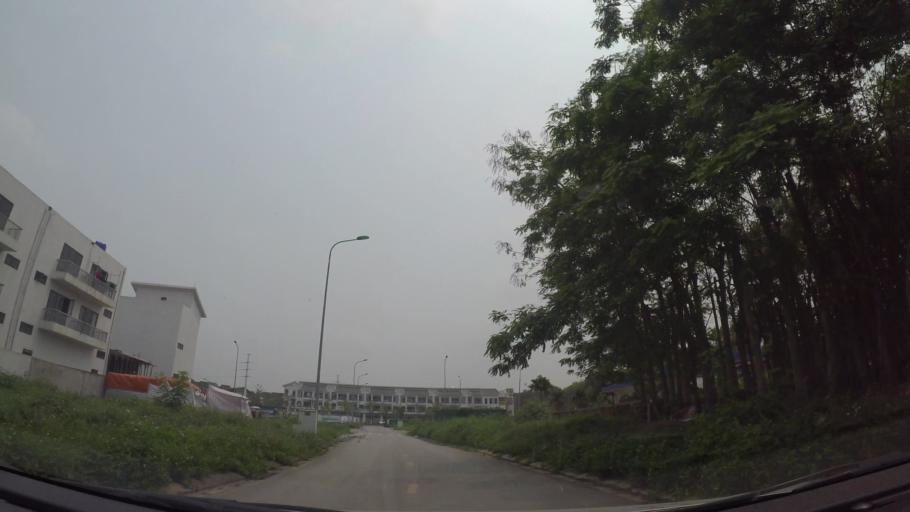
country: VN
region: Ha Noi
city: Cau Dien
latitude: 21.0273
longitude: 105.7418
